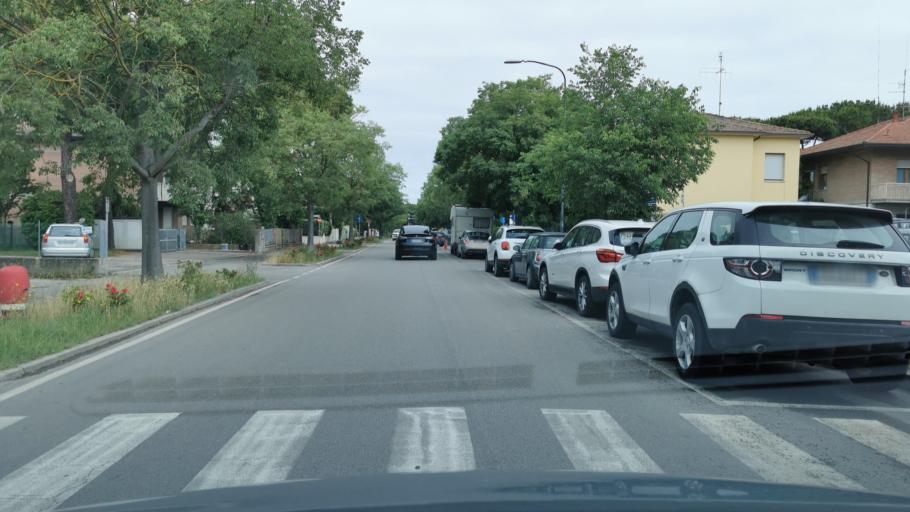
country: IT
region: Emilia-Romagna
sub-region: Provincia di Ravenna
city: Cervia
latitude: 44.2641
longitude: 12.3473
